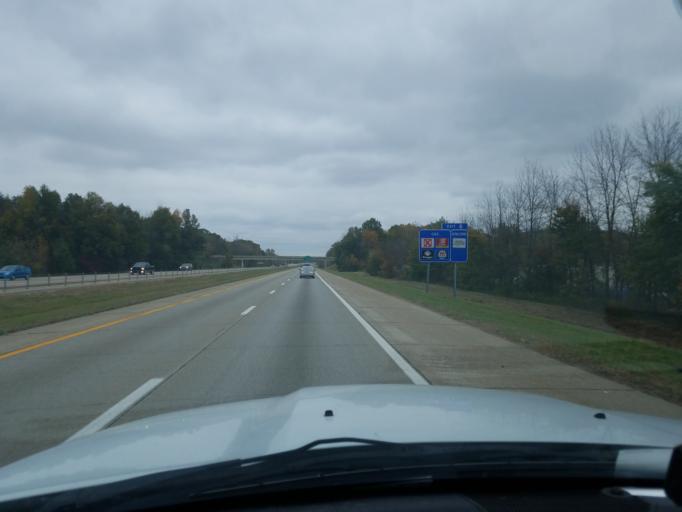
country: US
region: Kentucky
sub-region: Jefferson County
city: Fairdale
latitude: 38.1155
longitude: -85.7915
